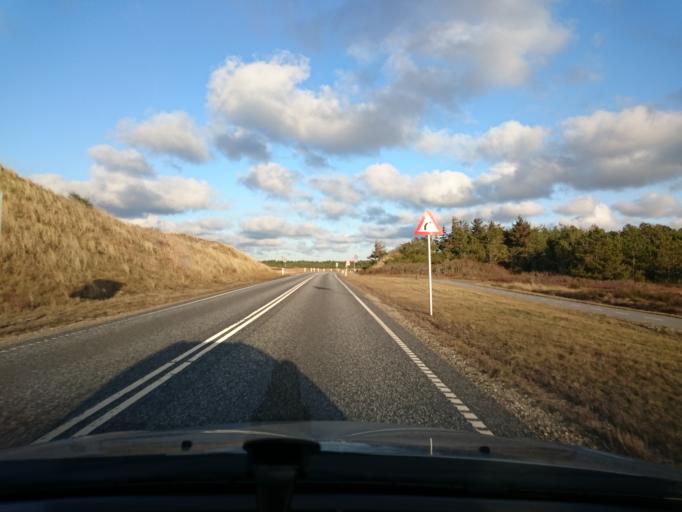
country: DK
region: North Denmark
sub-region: Frederikshavn Kommune
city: Skagen
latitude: 57.6950
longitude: 10.4757
